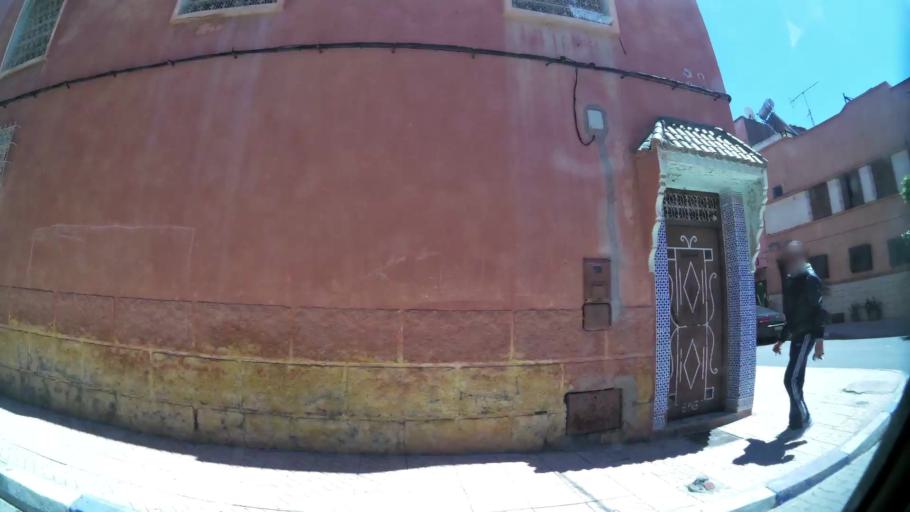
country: MA
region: Marrakech-Tensift-Al Haouz
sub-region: Marrakech
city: Marrakesh
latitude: 31.6484
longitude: -7.9916
